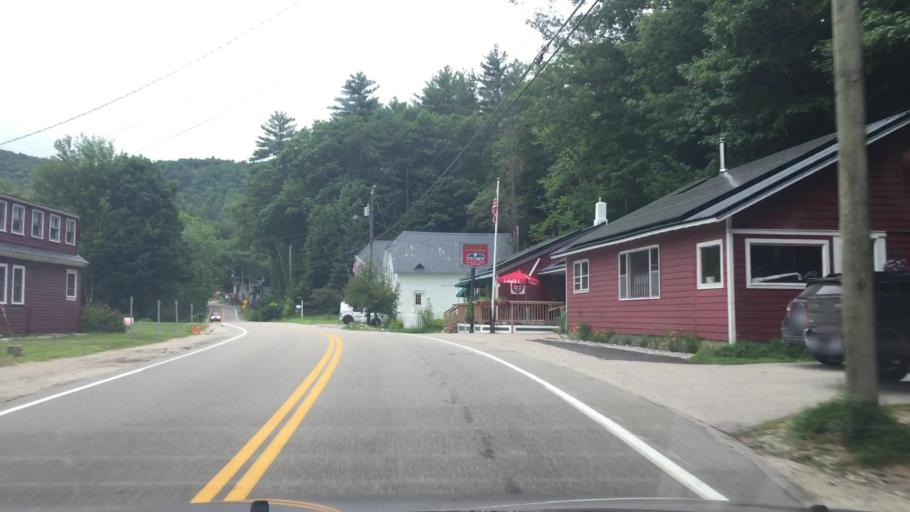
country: US
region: New Hampshire
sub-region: Carroll County
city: Madison
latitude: 43.9118
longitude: -71.0794
